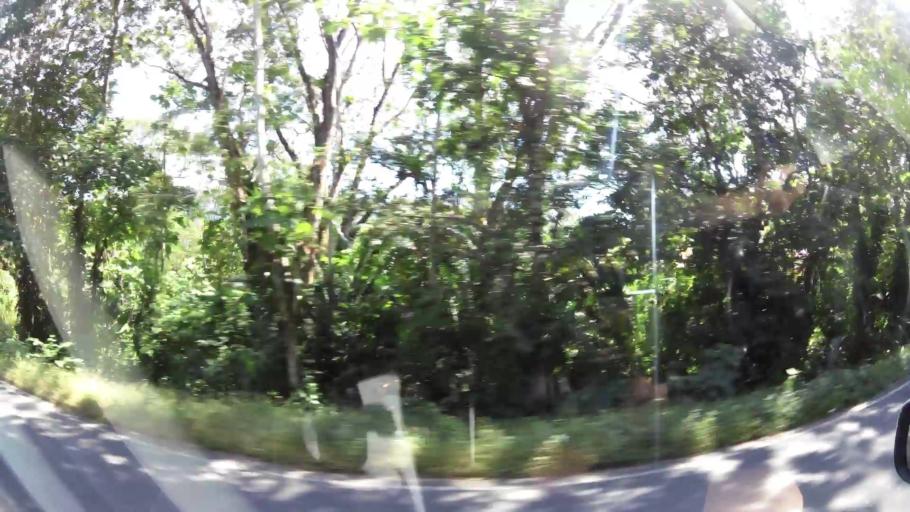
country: CR
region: San Jose
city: San Isidro
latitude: 9.2682
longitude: -83.8633
